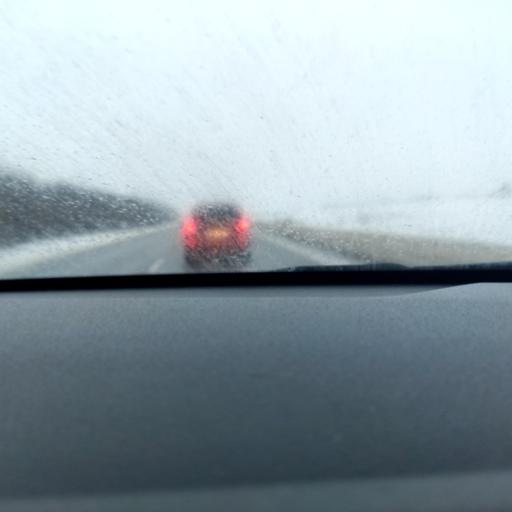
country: RU
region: Tatarstan
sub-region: Alekseyevskiy Rayon
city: Alekseyevskoye
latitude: 55.3131
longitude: 50.2475
